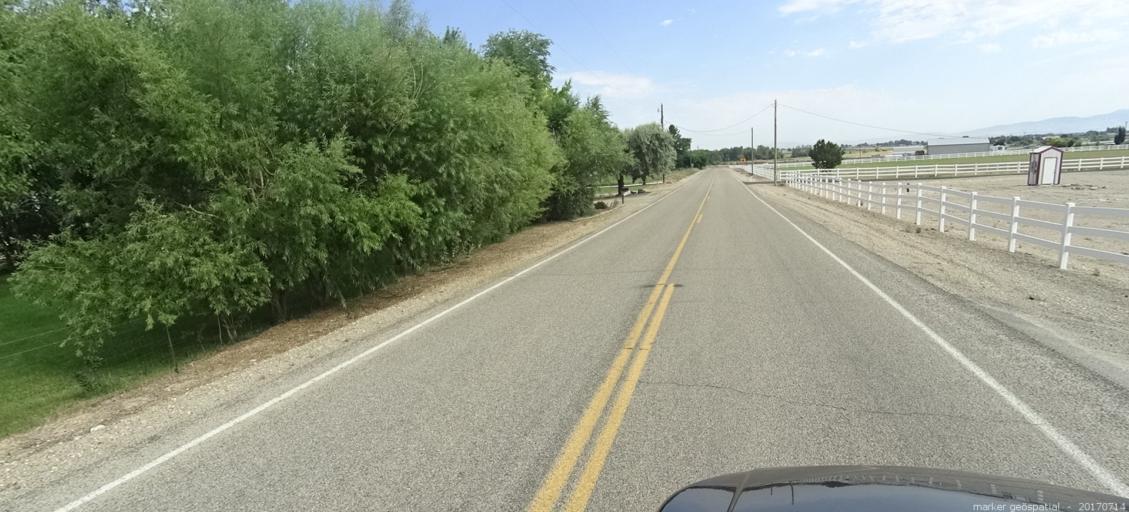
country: US
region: Idaho
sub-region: Ada County
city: Kuna
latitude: 43.4990
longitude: -116.3543
